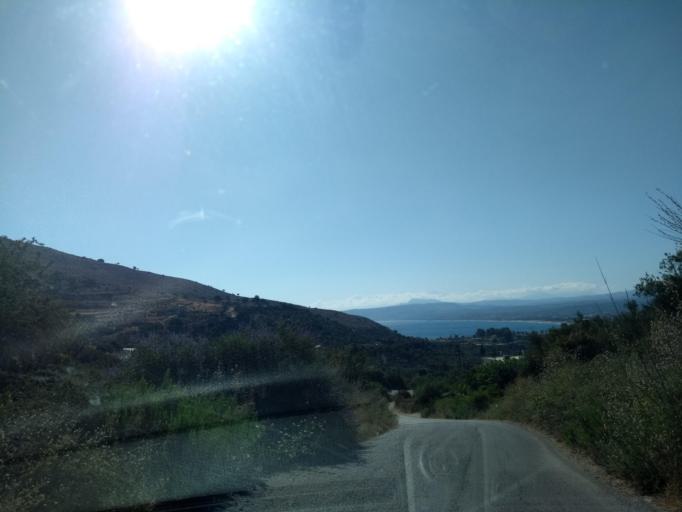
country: GR
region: Crete
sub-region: Nomos Chanias
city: Georgioupolis
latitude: 35.3718
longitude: 24.2445
